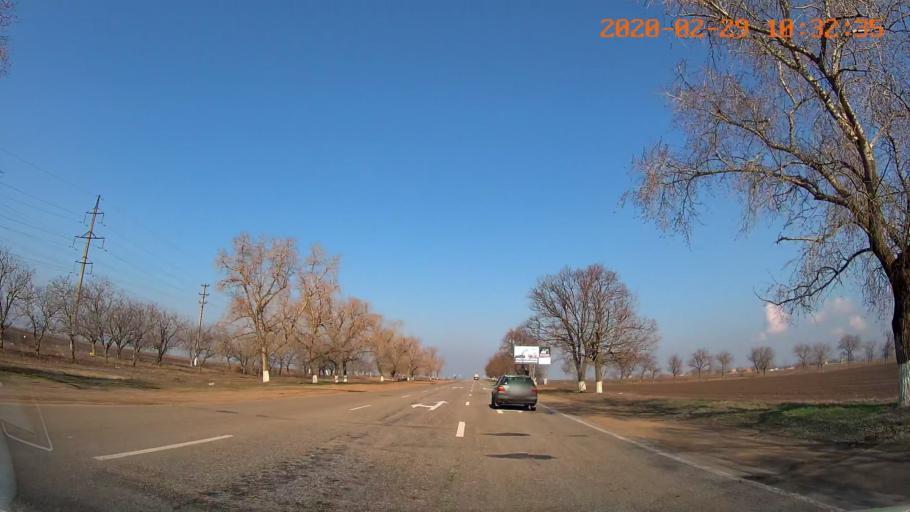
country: UA
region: Odessa
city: Velykoploske
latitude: 46.9625
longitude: 29.5528
